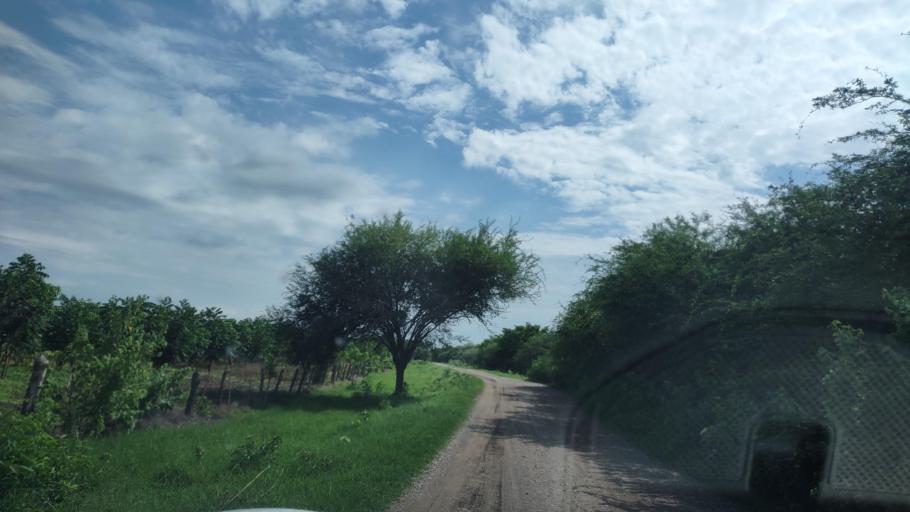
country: MX
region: Veracruz
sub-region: Panuco
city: Oviedo
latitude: 22.0003
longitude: -98.4592
